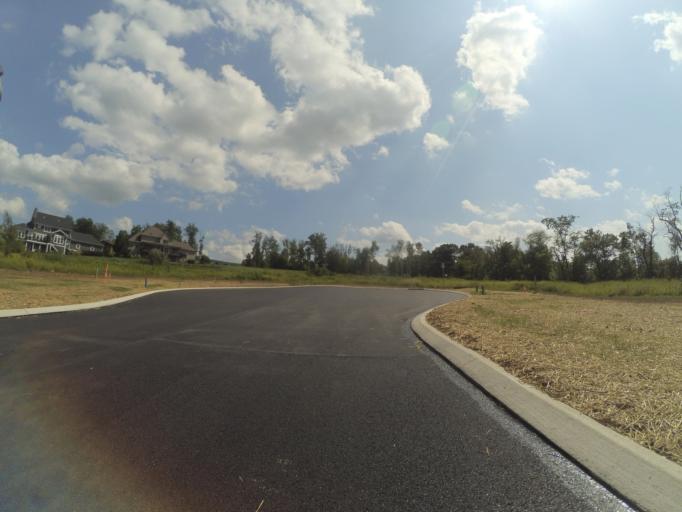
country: US
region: Pennsylvania
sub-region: Centre County
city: Houserville
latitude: 40.8275
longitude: -77.8222
